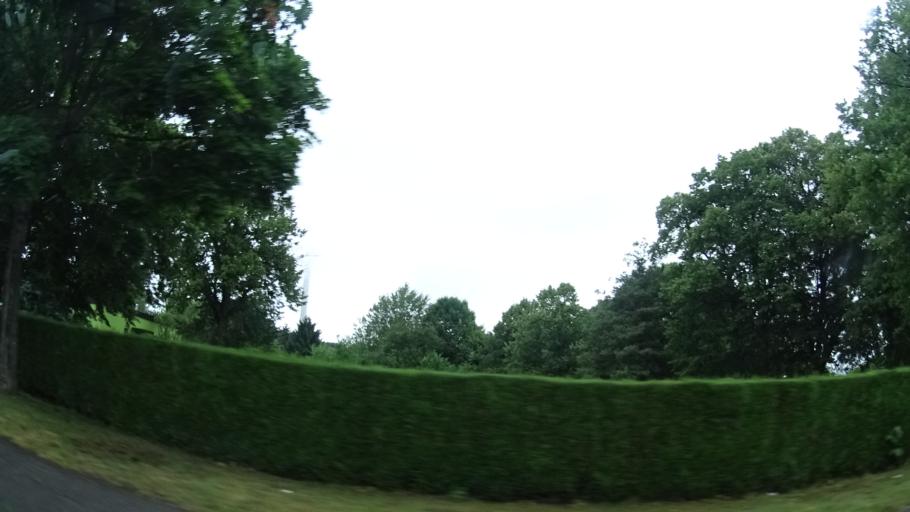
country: DE
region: Saarland
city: Quierschied
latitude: 49.3267
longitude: 7.0381
